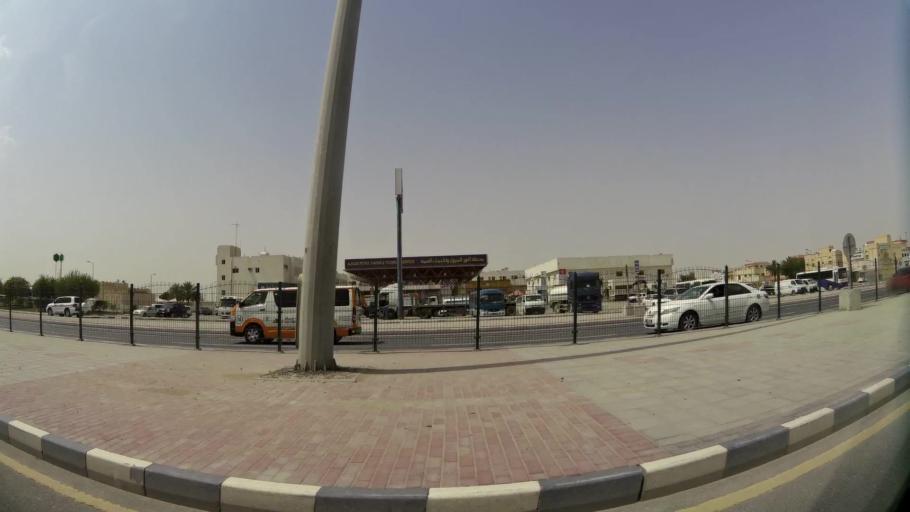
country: QA
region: Baladiyat ar Rayyan
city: Ar Rayyan
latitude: 25.2400
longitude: 51.4313
